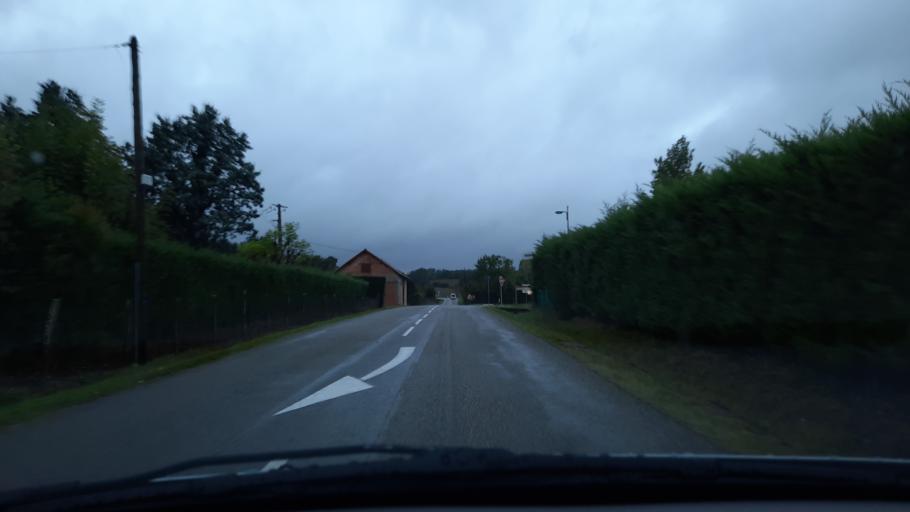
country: FR
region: Midi-Pyrenees
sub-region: Departement du Tarn-et-Garonne
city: Lafrancaise
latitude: 44.1926
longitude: 1.2849
